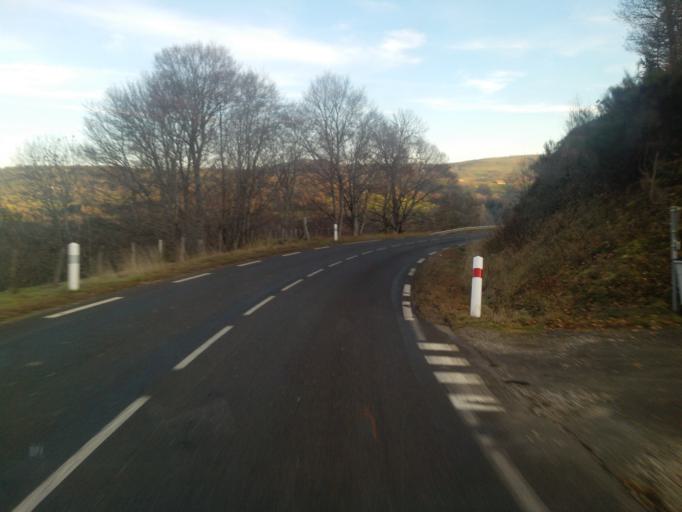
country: FR
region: Auvergne
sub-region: Departement du Cantal
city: Riom-es-Montagnes
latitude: 45.2554
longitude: 2.7050
